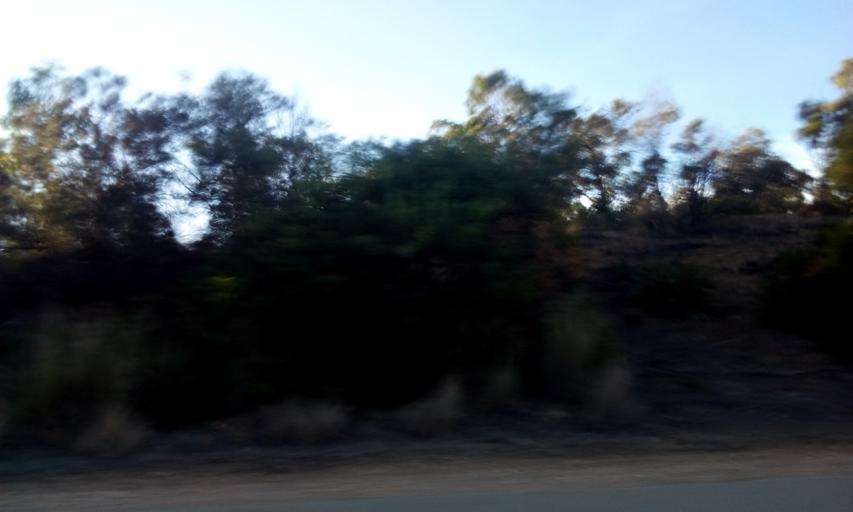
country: AU
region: New South Wales
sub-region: Yass Valley
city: Gundaroo
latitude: -35.1065
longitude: 149.3717
